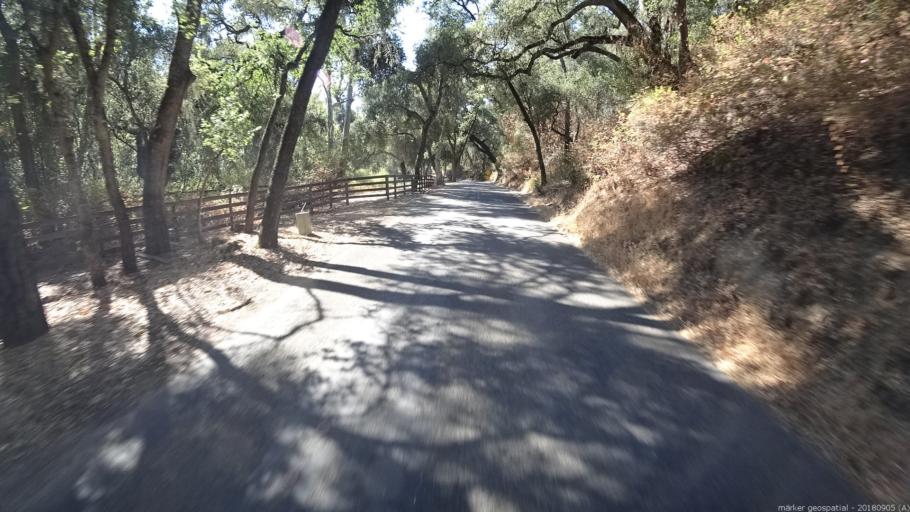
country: US
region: California
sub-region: Monterey County
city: Gonzales
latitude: 36.3789
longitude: -121.5925
